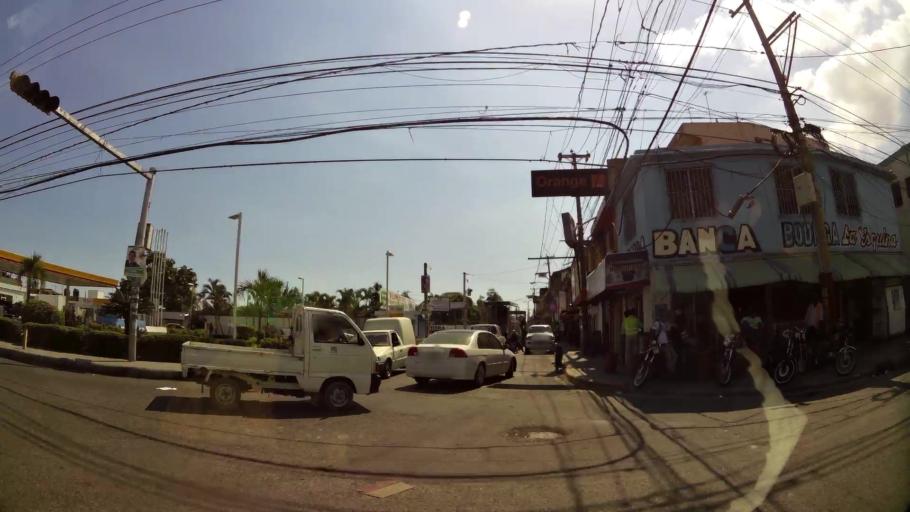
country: DO
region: Nacional
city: Santo Domingo
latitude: 18.4791
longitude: -69.9780
